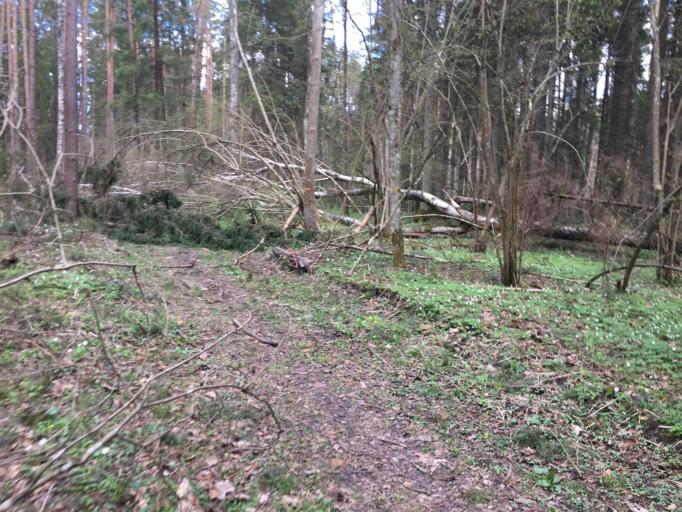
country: LV
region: Baldone
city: Baldone
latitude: 56.7501
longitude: 24.3814
